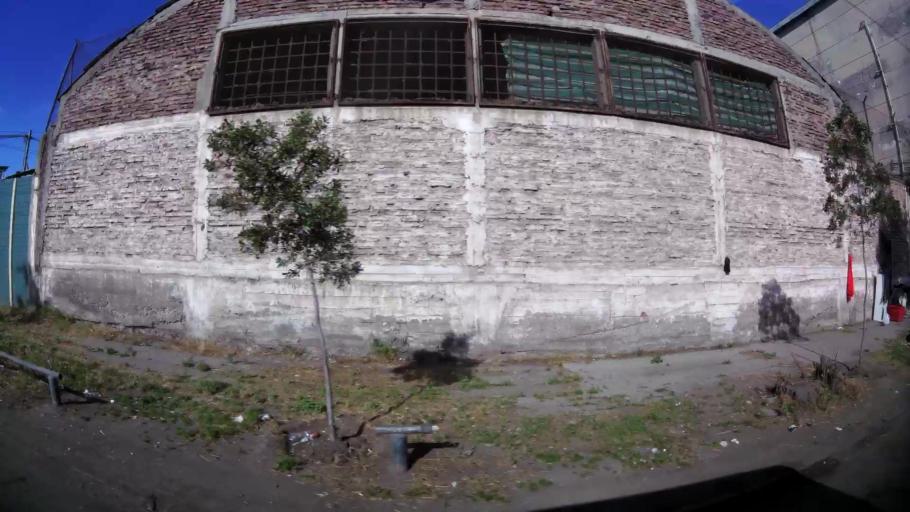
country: CL
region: Santiago Metropolitan
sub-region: Provincia de Santiago
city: Santiago
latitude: -33.4622
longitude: -70.6825
